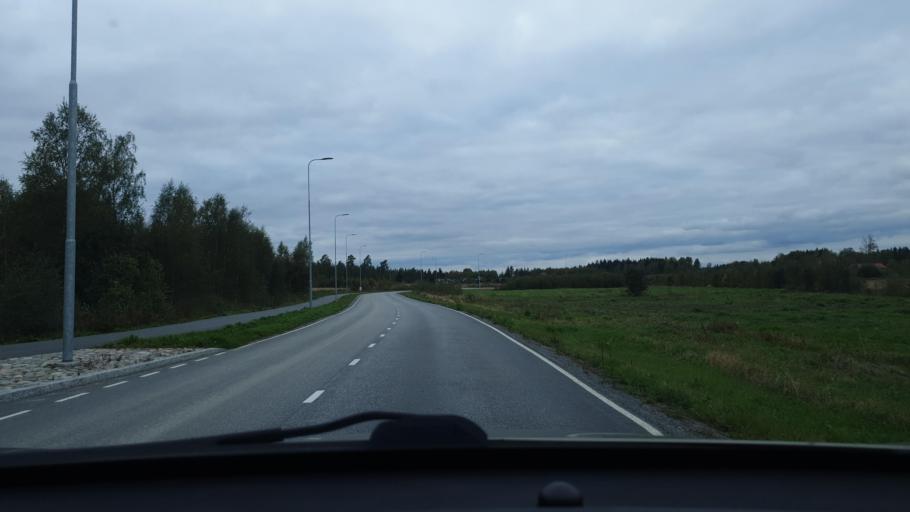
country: FI
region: Ostrobothnia
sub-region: Vaasa
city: Korsholm
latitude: 63.1280
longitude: 21.6638
